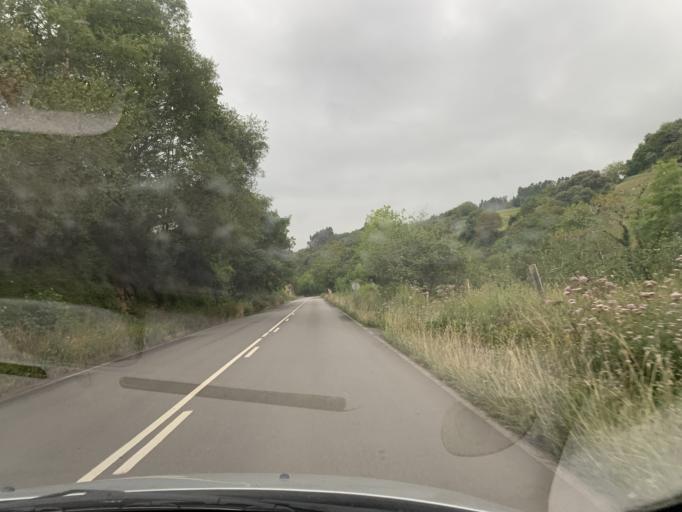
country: ES
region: Asturias
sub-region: Province of Asturias
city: Carrena
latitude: 43.3951
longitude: -4.9123
